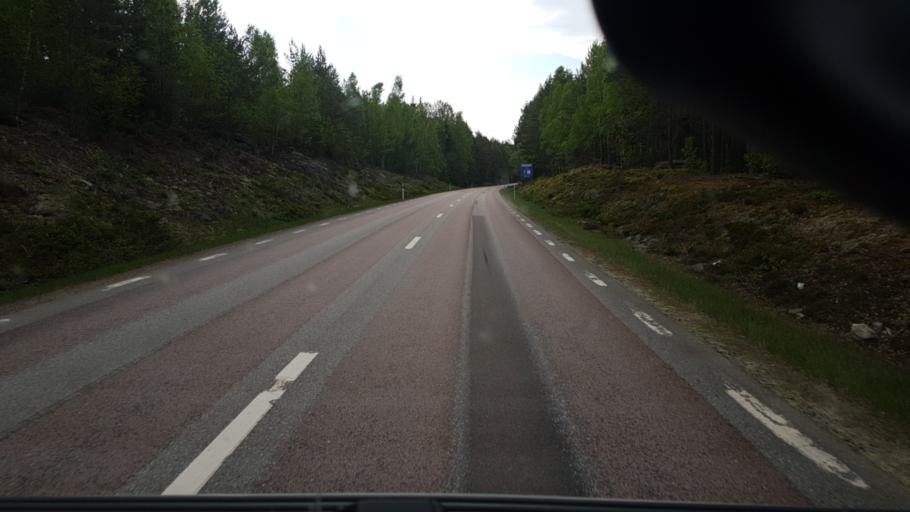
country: SE
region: Vaermland
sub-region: Arvika Kommun
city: Arvika
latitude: 59.5665
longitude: 12.7193
